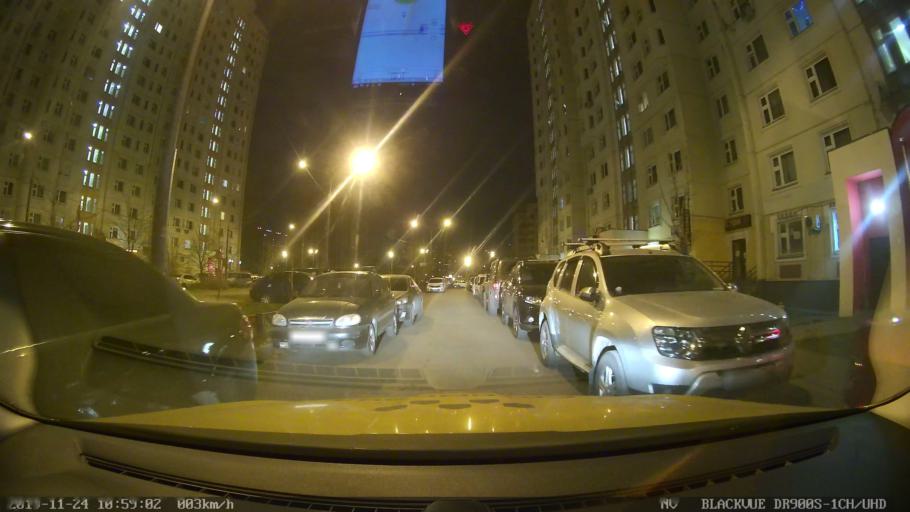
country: RU
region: Moskovskaya
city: Mytishchi
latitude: 55.9084
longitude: 37.7065
